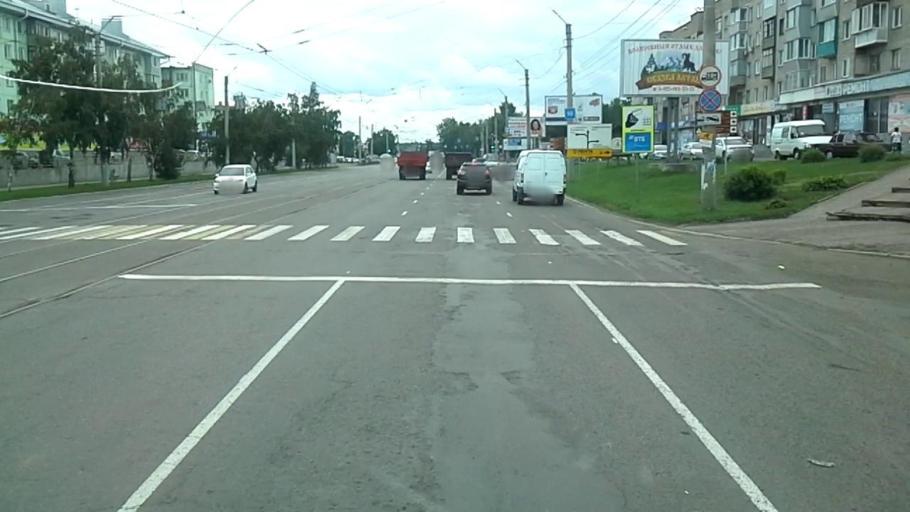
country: RU
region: Altai Krai
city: Biysk
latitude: 52.5430
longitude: 85.2180
